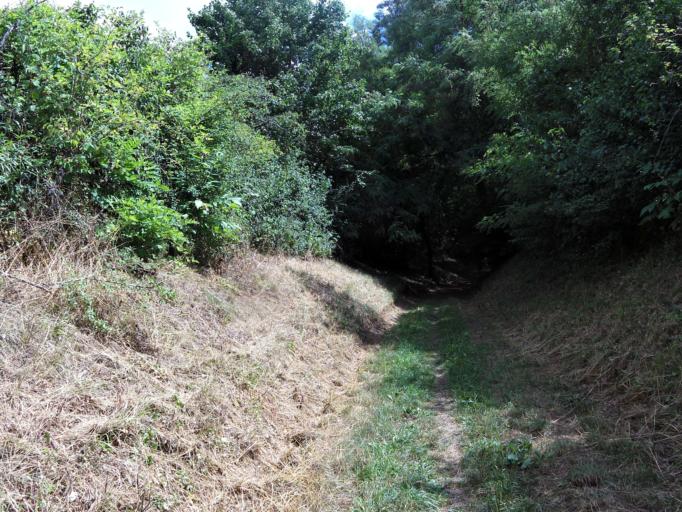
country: DE
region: Bavaria
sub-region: Regierungsbezirk Unterfranken
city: Gerbrunn
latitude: 49.7743
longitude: 9.9979
